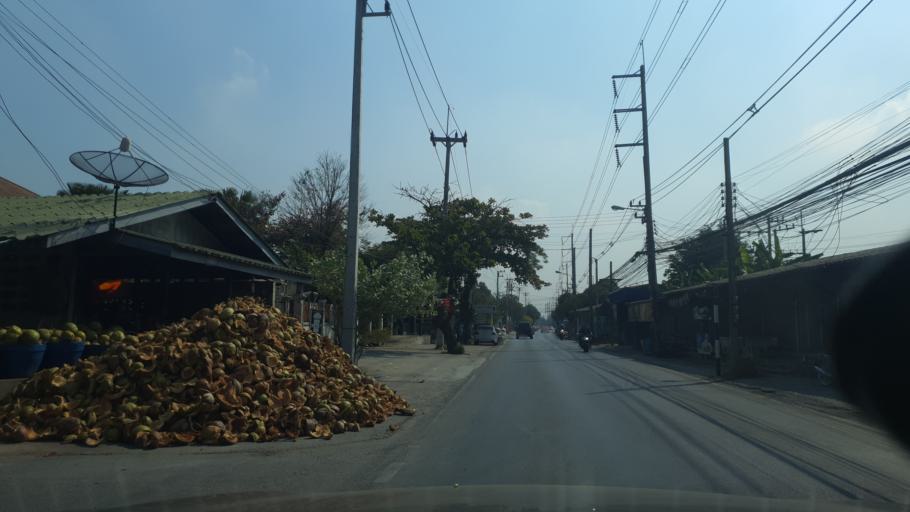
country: TH
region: Nakhon Pathom
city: Salaya
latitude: 13.7747
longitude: 100.2792
